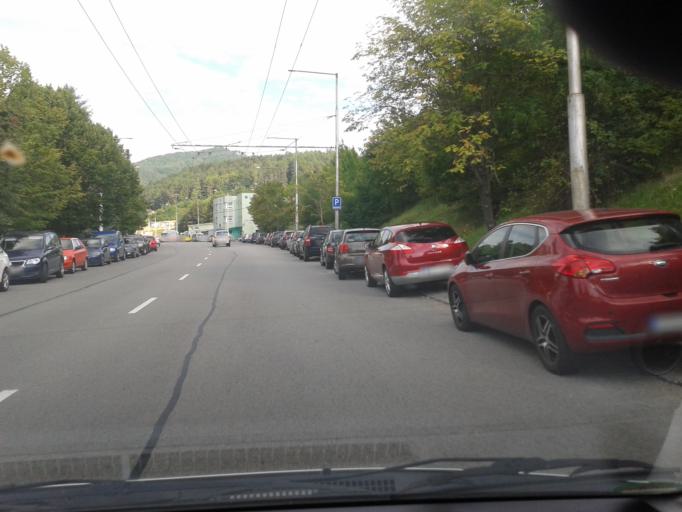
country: SK
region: Banskobystricky
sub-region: Okres Banska Bystrica
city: Banska Bystrica
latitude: 48.7437
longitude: 19.1214
